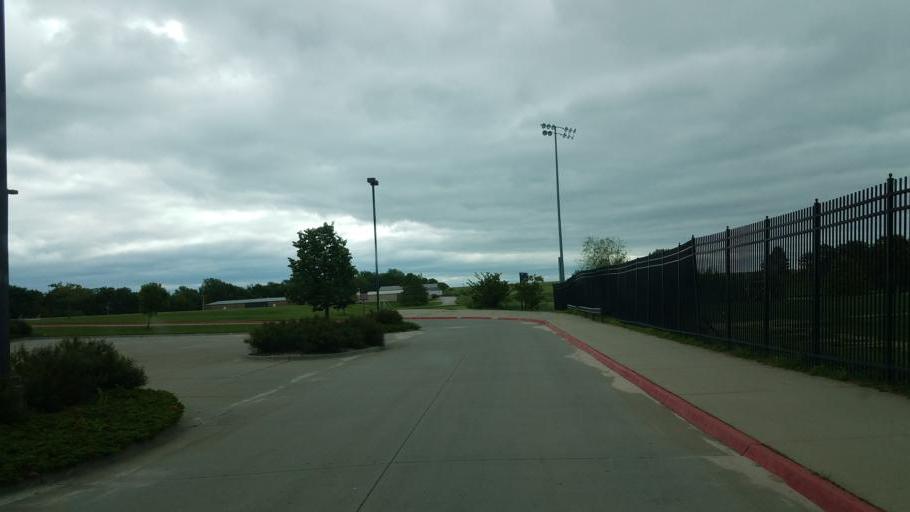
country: US
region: Iowa
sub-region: Decatur County
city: Lamoni
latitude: 40.6150
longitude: -93.9236
